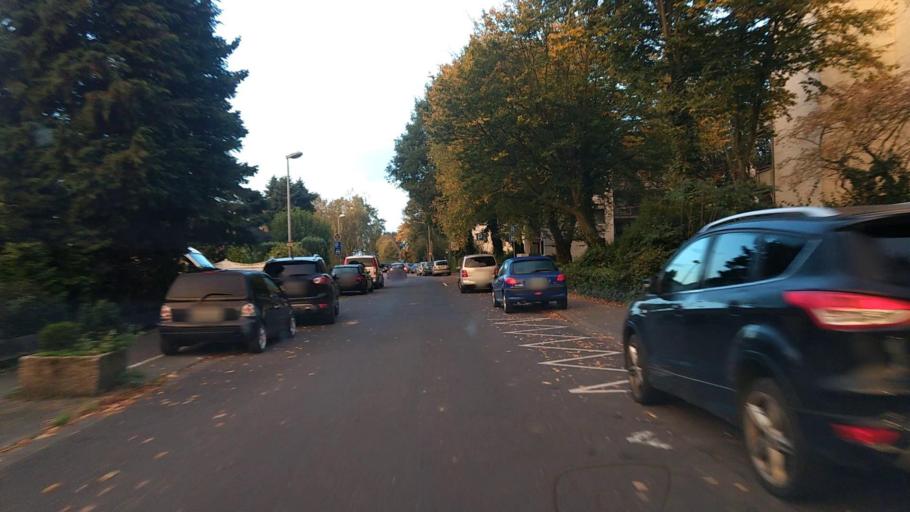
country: DE
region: North Rhine-Westphalia
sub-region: Regierungsbezirk Koln
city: Bergheim
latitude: 50.9250
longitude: 6.6551
